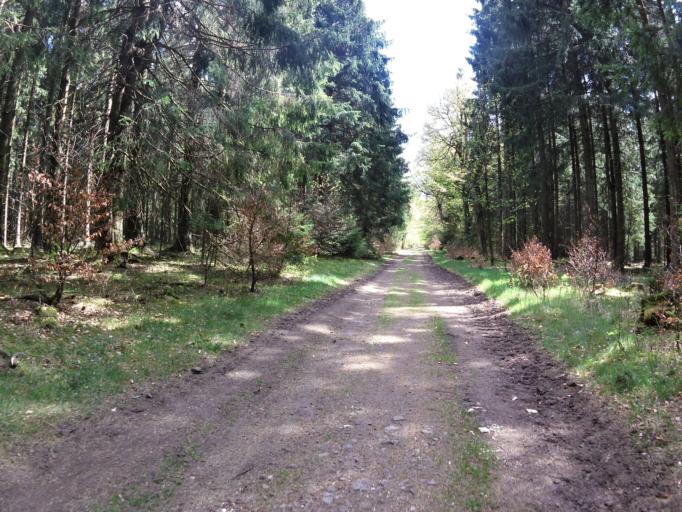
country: DE
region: Thuringia
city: Friedrichroda
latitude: 50.8260
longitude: 10.5387
